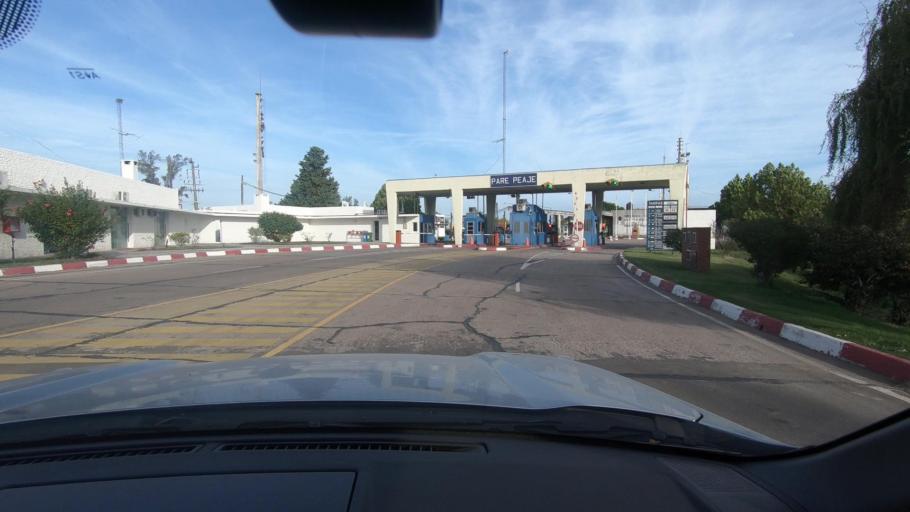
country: AR
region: Entre Rios
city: Colon
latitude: -32.2490
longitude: -58.1430
